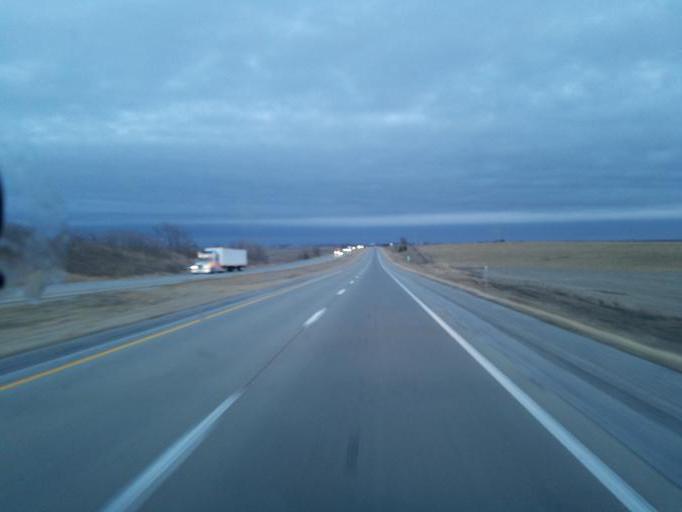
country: US
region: Iowa
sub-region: Pottawattamie County
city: Avoca
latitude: 41.4980
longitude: -95.1698
